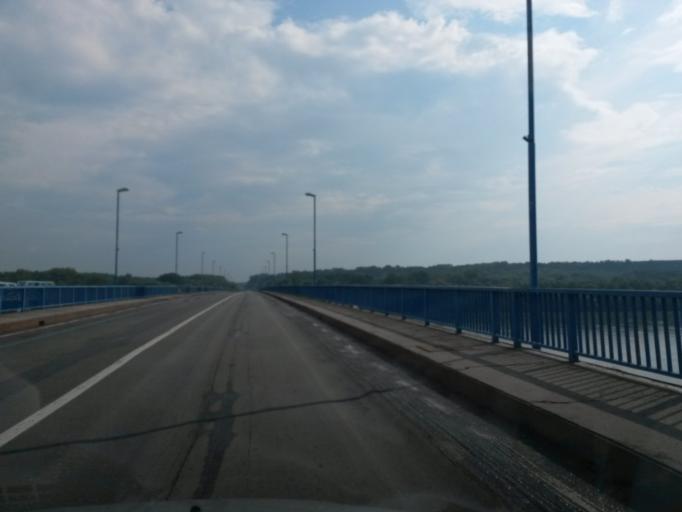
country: RS
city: Bogojevo
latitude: 45.5261
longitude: 19.0856
